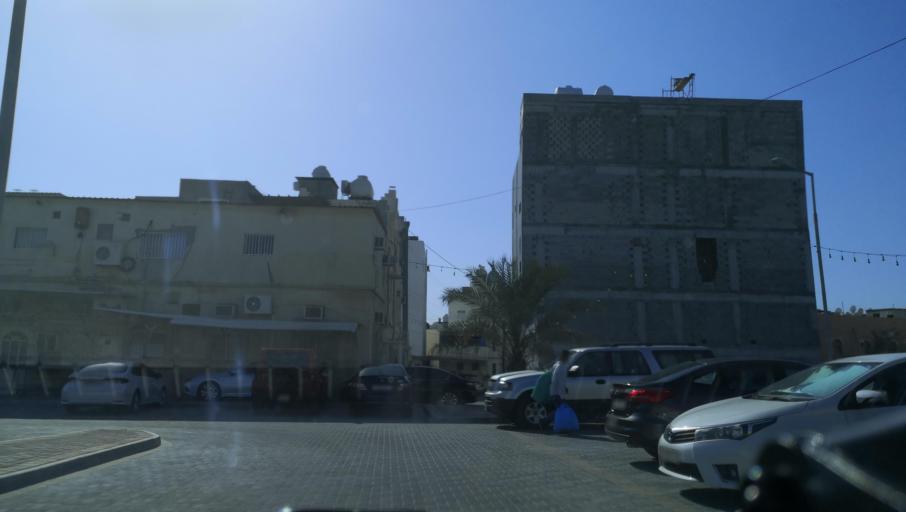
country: BH
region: Muharraq
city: Al Muharraq
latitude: 26.2531
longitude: 50.6321
